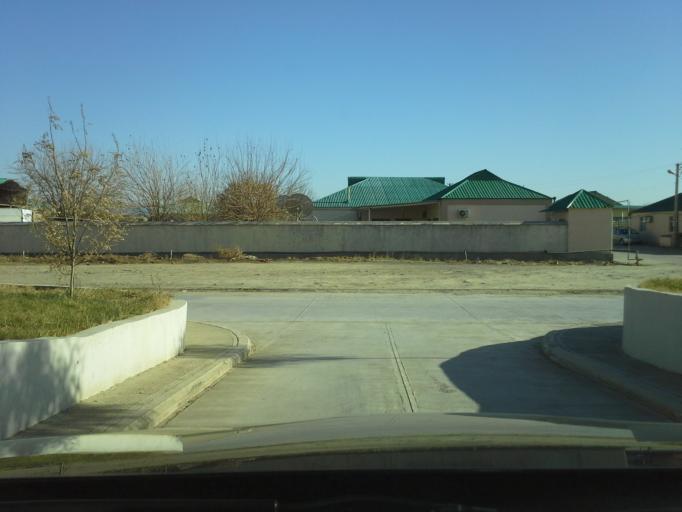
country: TM
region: Ahal
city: Ashgabat
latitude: 37.9715
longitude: 58.3399
